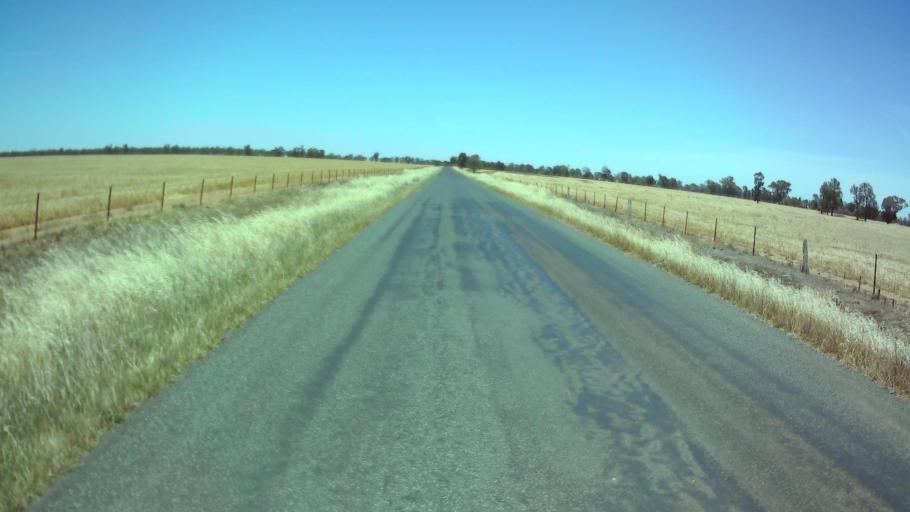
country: AU
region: New South Wales
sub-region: Weddin
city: Grenfell
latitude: -34.0490
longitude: 147.7820
